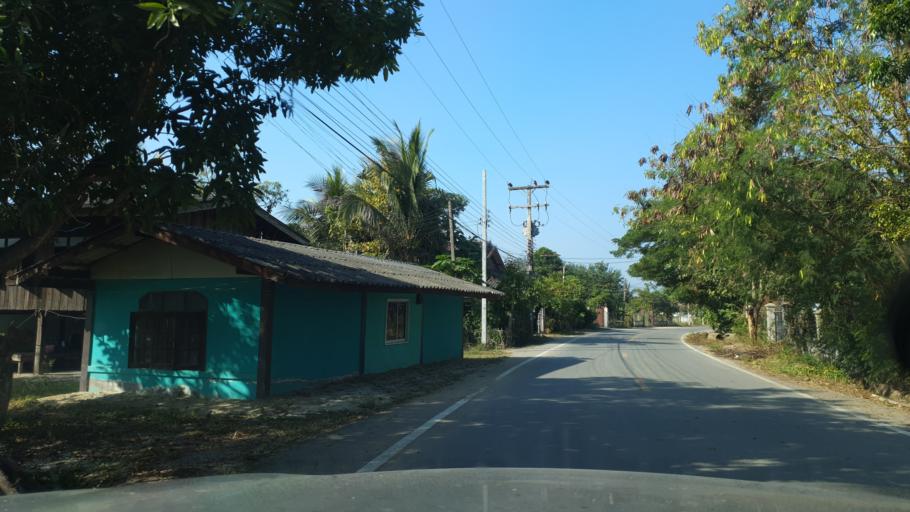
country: TH
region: Lamphun
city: Ban Thi
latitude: 18.6823
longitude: 99.1214
